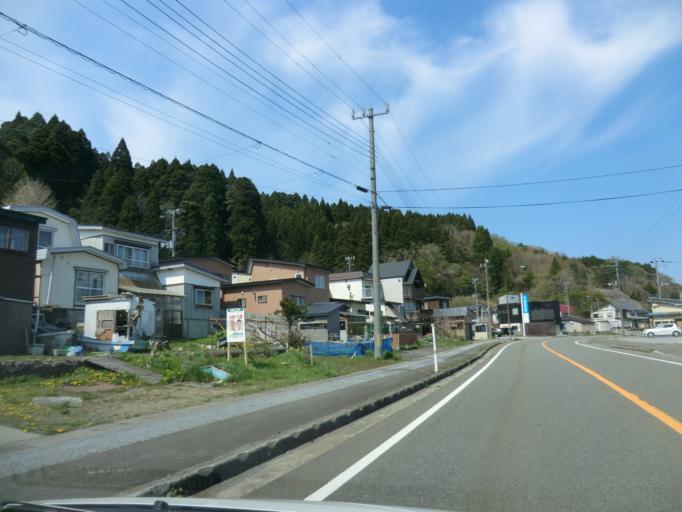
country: JP
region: Aomori
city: Mutsu
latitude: 41.4678
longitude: 141.0927
